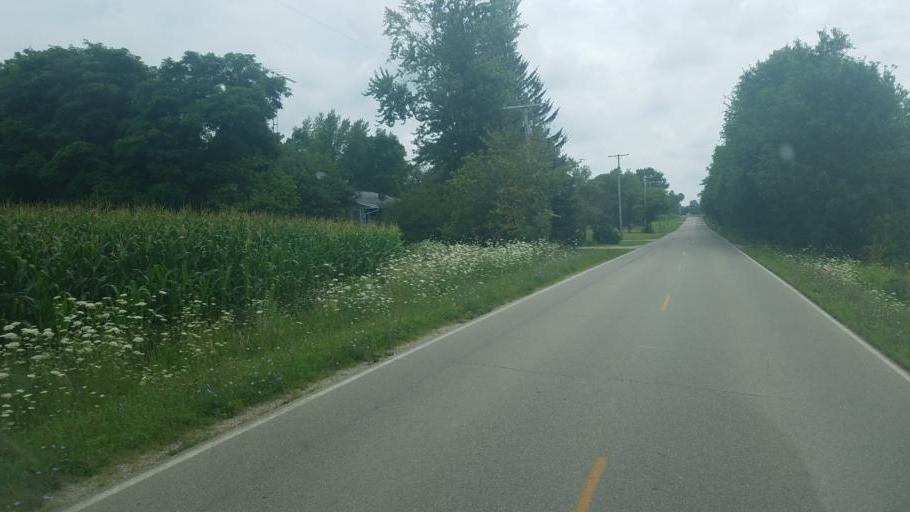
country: US
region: Ohio
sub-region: Crawford County
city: Crestline
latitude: 40.7331
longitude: -82.7321
